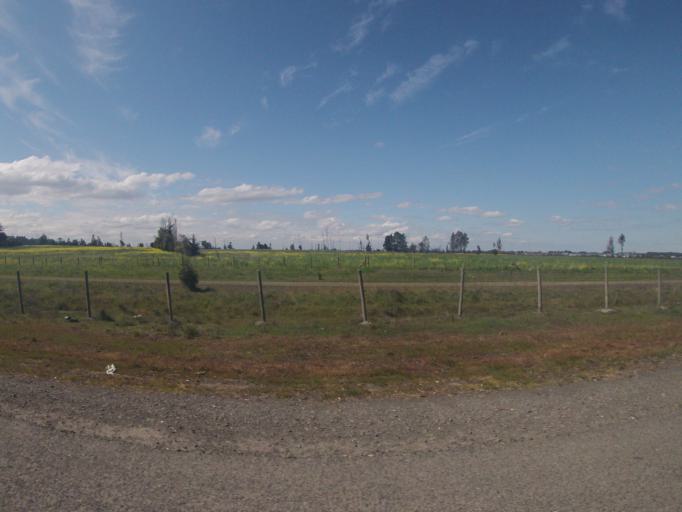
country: CL
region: Biobio
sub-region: Provincia de Biobio
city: Los Angeles
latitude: -37.4489
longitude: -72.4065
